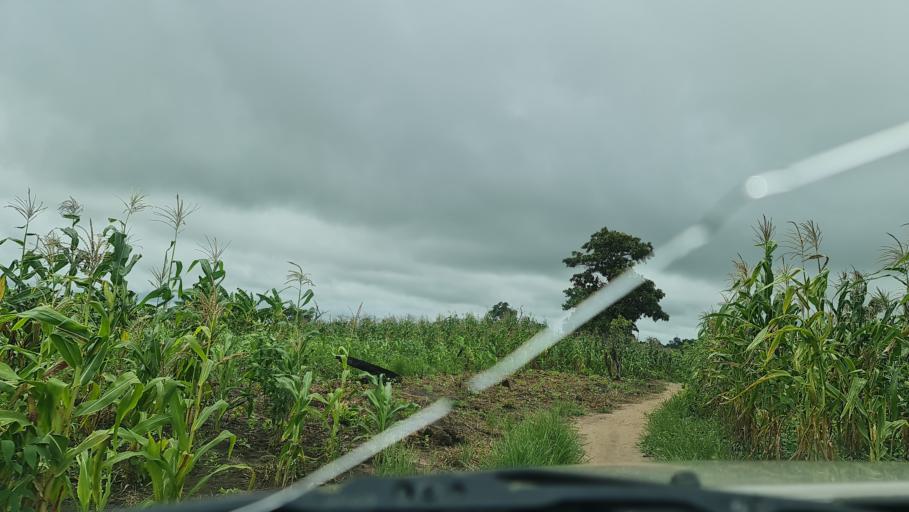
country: MW
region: Southern Region
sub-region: Nsanje District
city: Nsanje
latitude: -17.3394
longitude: 35.7236
